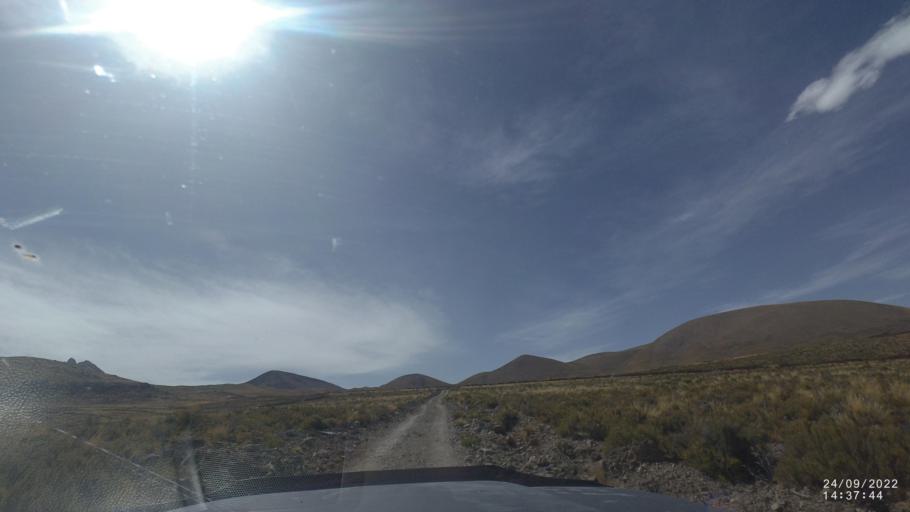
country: BO
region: Potosi
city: Colchani
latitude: -19.8545
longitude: -67.5835
